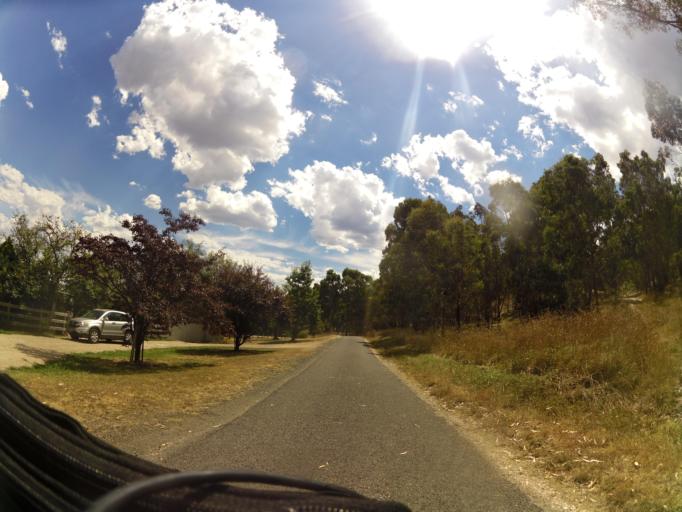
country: AU
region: Victoria
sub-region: Wellington
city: Heyfield
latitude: -37.9788
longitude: 146.7779
